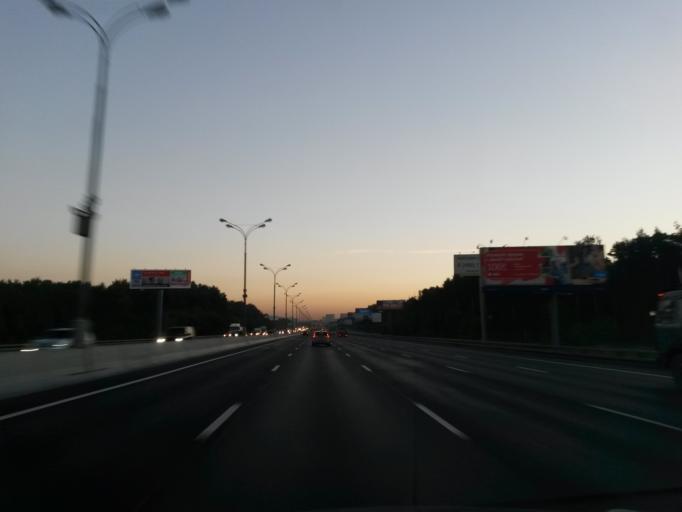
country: RU
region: Moscow
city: Zhulebino
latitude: 55.6715
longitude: 37.8365
